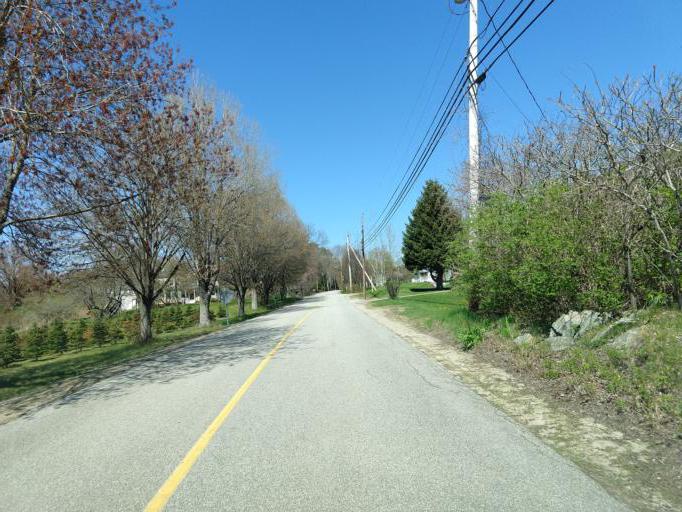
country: US
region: Maine
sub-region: York County
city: Arundel
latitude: 43.3755
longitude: -70.4747
